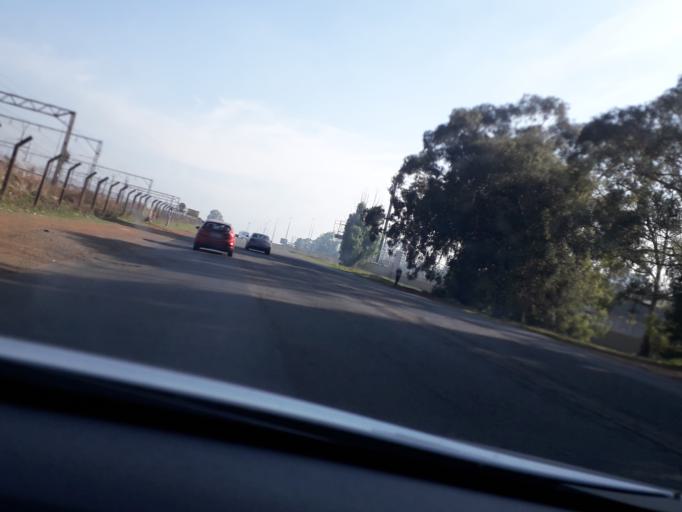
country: ZA
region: Gauteng
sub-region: Ekurhuleni Metropolitan Municipality
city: Boksburg
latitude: -26.1467
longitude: 28.2182
